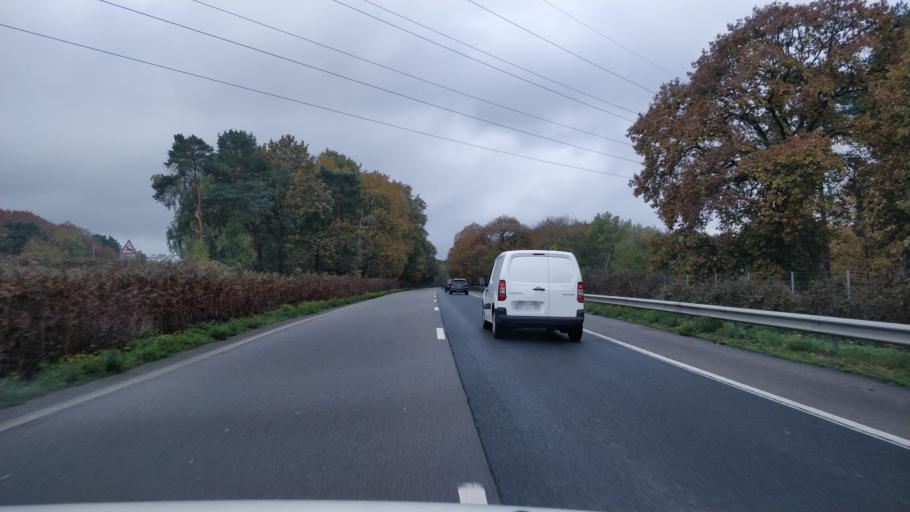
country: FR
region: Haute-Normandie
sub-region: Departement de la Seine-Maritime
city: Grand-Couronne
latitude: 49.3587
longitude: 1.0341
